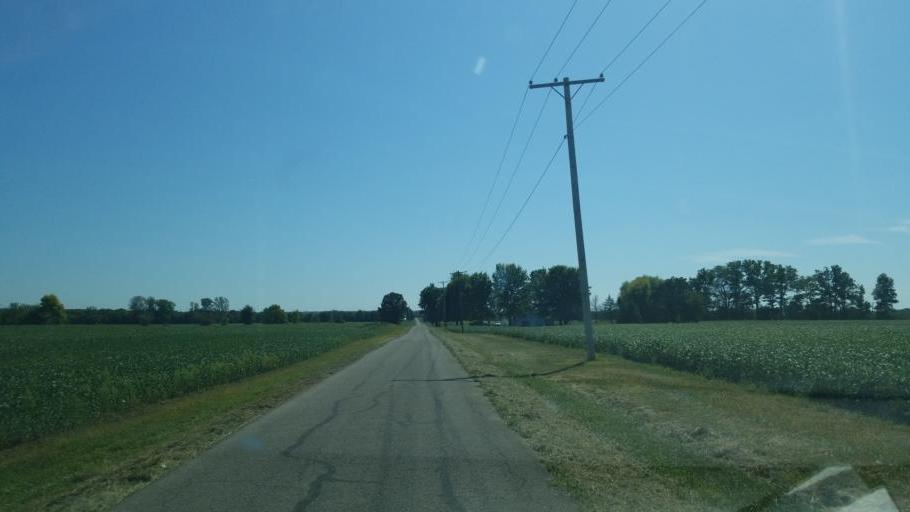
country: US
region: Ohio
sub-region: Logan County
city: Northwood
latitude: 40.5089
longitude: -83.7684
